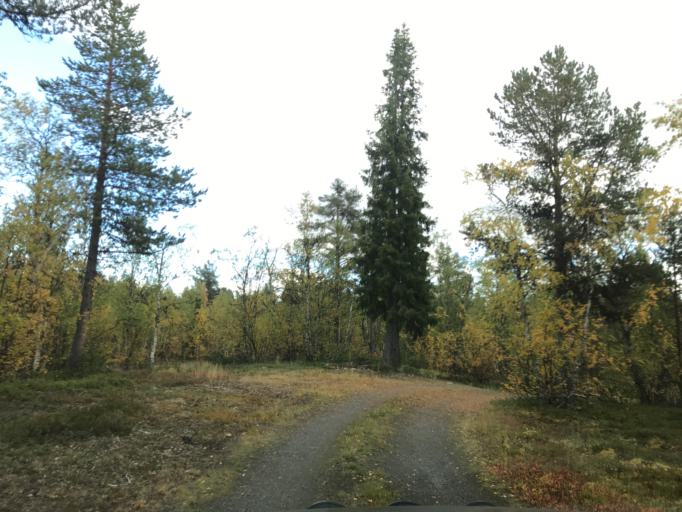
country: SE
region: Norrbotten
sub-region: Gallivare Kommun
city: Malmberget
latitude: 67.5845
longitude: 20.8537
